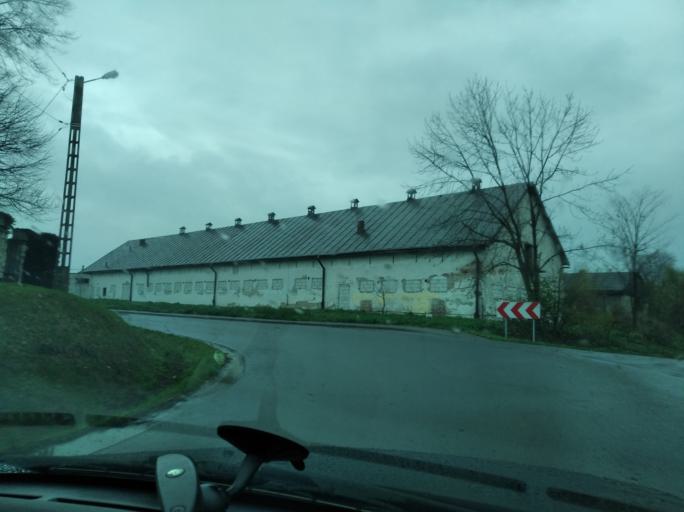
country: PL
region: Subcarpathian Voivodeship
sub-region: Powiat lancucki
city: Wysoka
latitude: 50.0429
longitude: 22.2387
